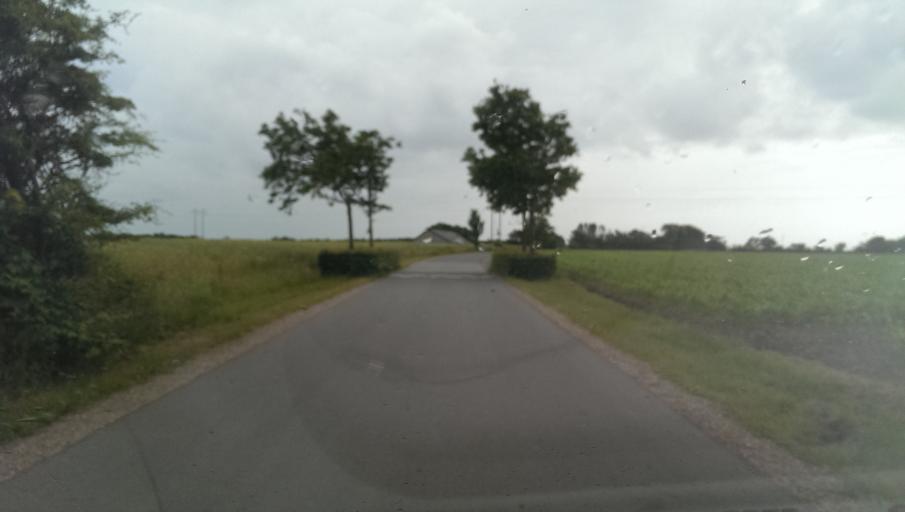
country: DK
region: South Denmark
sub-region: Esbjerg Kommune
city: Bramming
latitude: 55.4300
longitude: 8.7159
